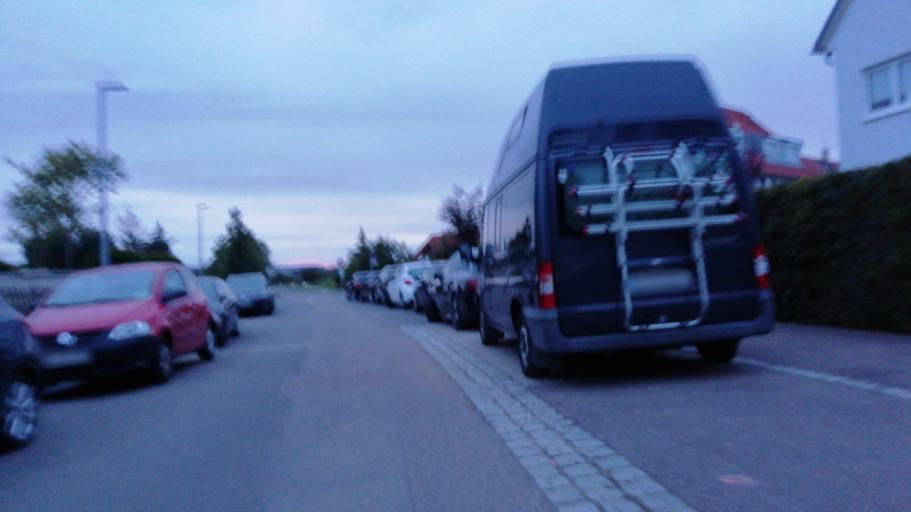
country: DE
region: Baden-Wuerttemberg
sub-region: Regierungsbezirk Stuttgart
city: Korntal
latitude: 48.8166
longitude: 9.1062
